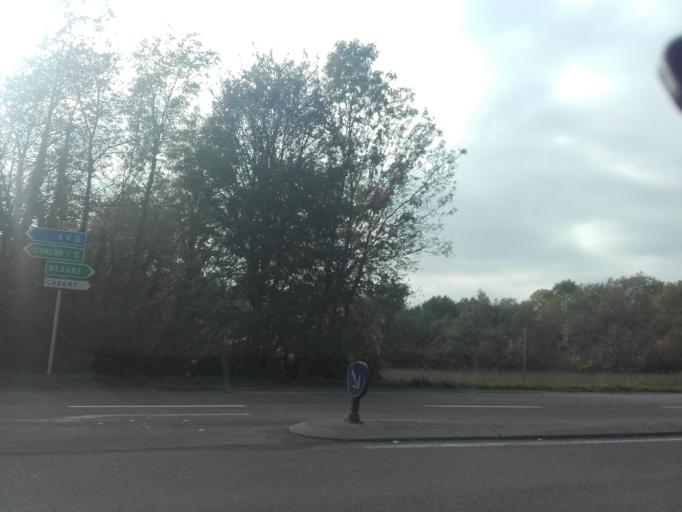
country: FR
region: Bourgogne
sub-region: Departement de Saone-et-Loire
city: Fontaines
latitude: 46.8806
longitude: 4.7793
